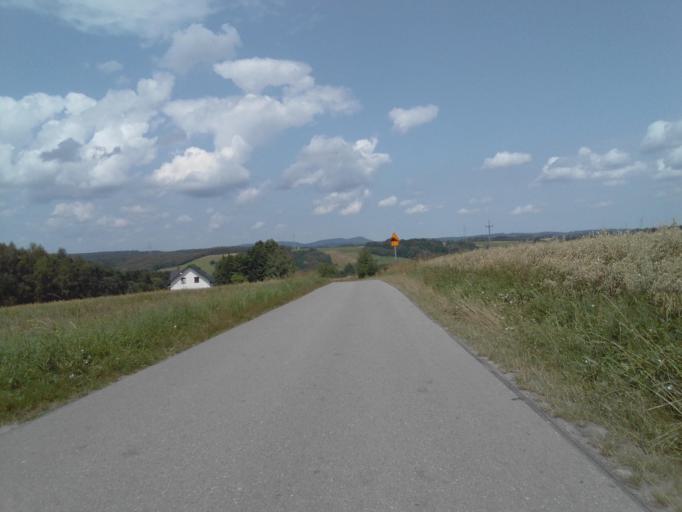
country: PL
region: Subcarpathian Voivodeship
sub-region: Powiat strzyzowski
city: Frysztak
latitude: 49.8002
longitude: 21.5948
